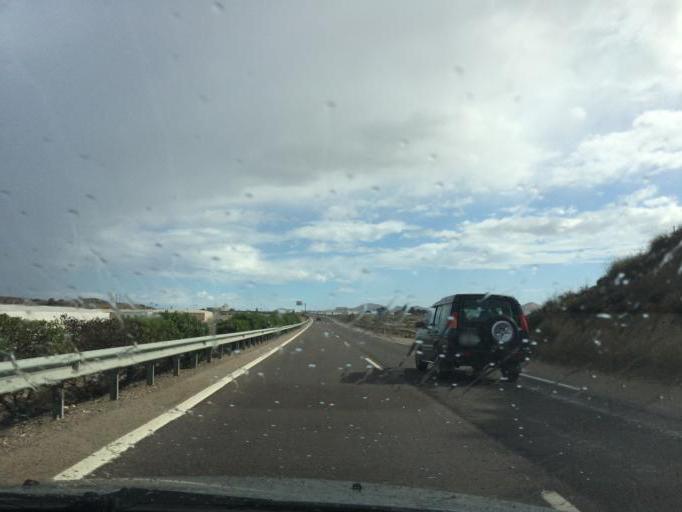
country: ES
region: Andalusia
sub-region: Provincia de Almeria
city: Retamar
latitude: 36.8663
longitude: -2.2383
